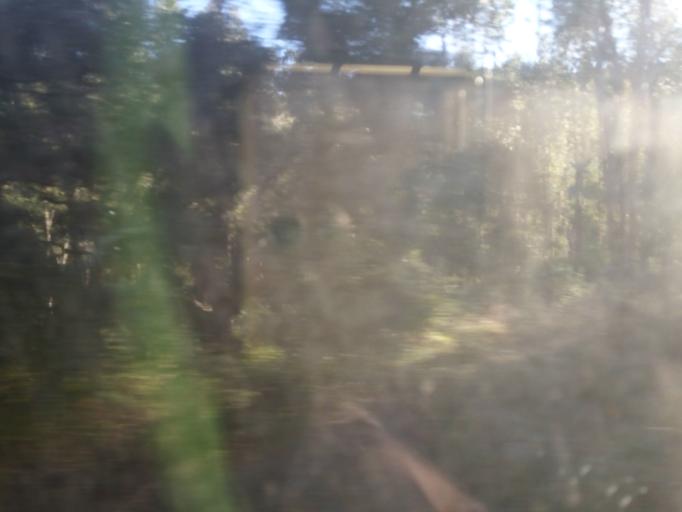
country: PT
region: Beja
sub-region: Odemira
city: Odemira
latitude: 37.6534
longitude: -8.4765
